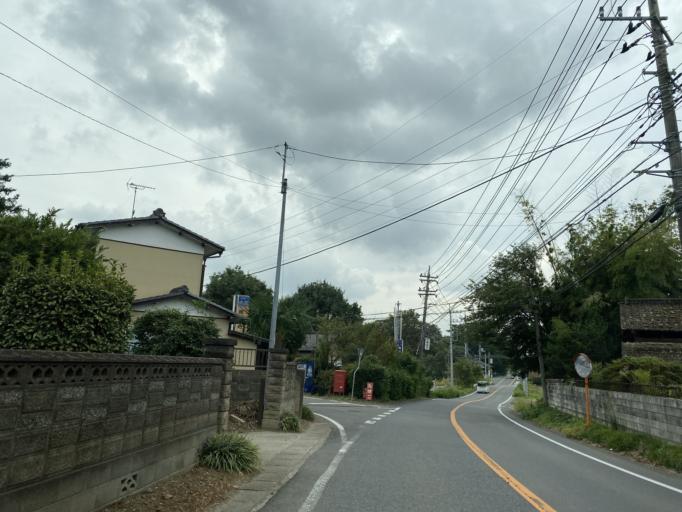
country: JP
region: Ibaraki
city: Mitsukaido
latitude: 35.9869
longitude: 140.0436
